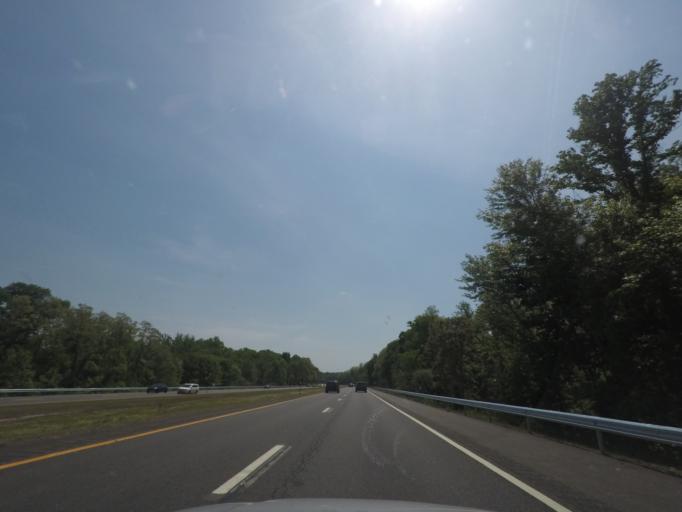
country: US
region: New York
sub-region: Rockland County
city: Chestnut Ridge
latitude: 41.0848
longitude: -74.0450
